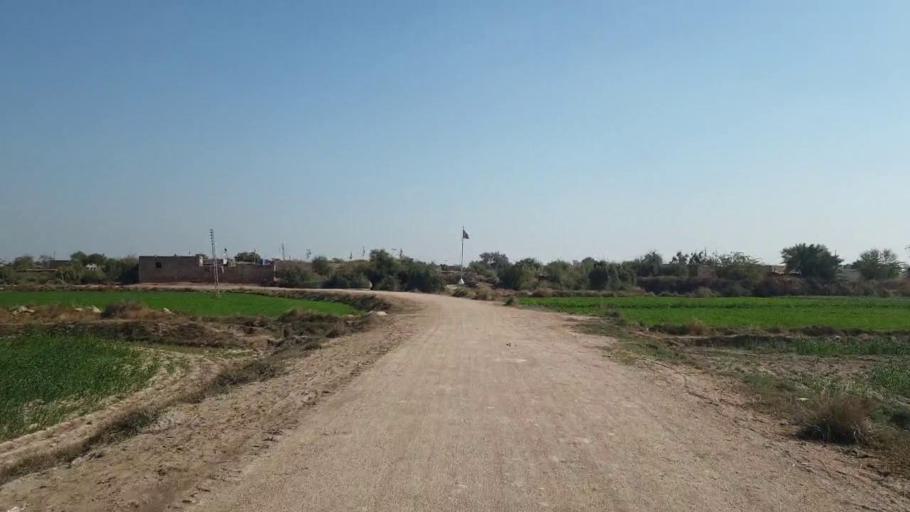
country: PK
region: Sindh
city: Shahdadpur
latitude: 25.9508
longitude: 68.6565
